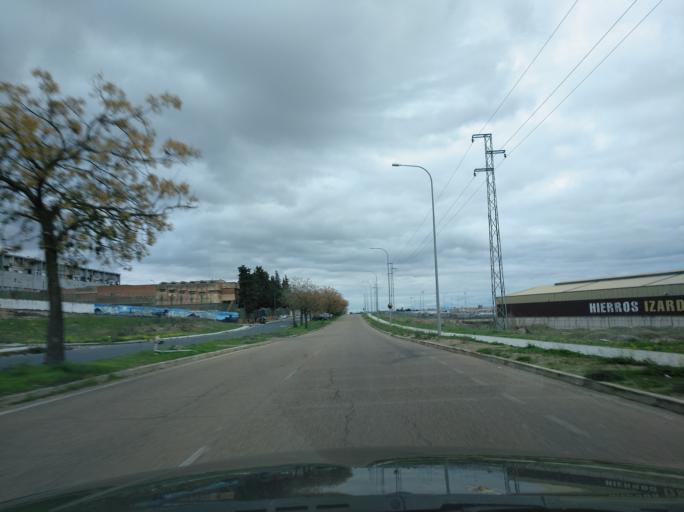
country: ES
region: Extremadura
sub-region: Provincia de Badajoz
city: Badajoz
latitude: 38.8977
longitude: -6.9857
